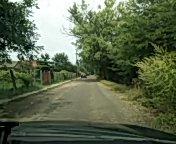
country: HU
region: Hajdu-Bihar
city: Debrecen
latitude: 47.5281
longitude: 21.7147
